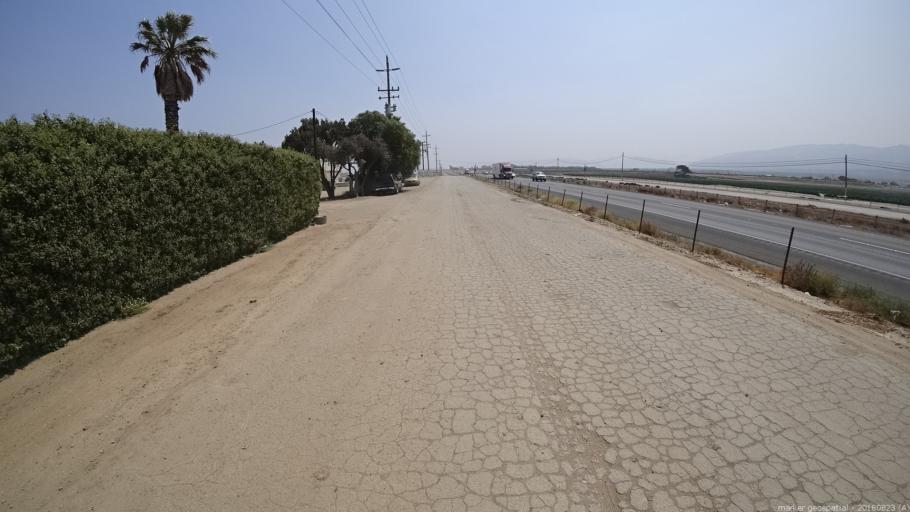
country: US
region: California
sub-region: Monterey County
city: Soledad
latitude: 36.3996
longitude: -121.3136
